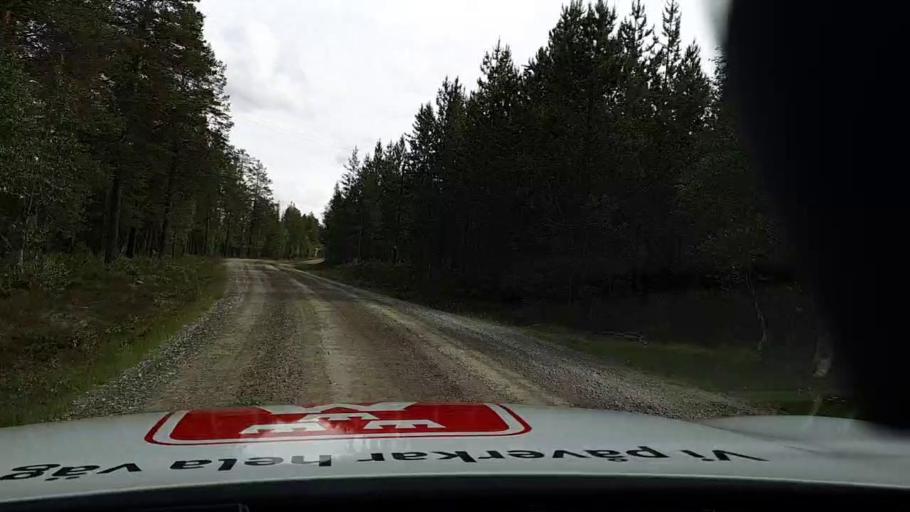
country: SE
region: Jaemtland
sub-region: Are Kommun
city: Jarpen
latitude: 62.4967
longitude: 13.5018
